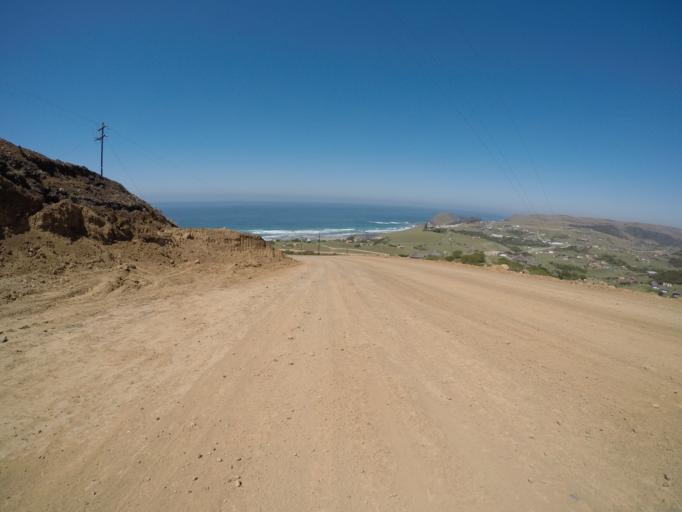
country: ZA
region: Eastern Cape
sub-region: OR Tambo District Municipality
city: Libode
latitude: -32.0244
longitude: 29.1149
